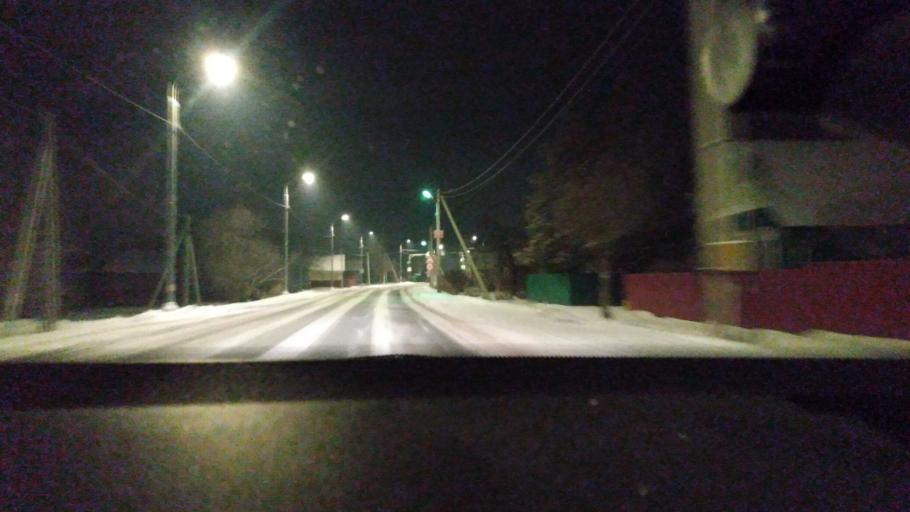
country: RU
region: Moskovskaya
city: Krasnaya Poyma
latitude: 55.1011
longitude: 38.9906
